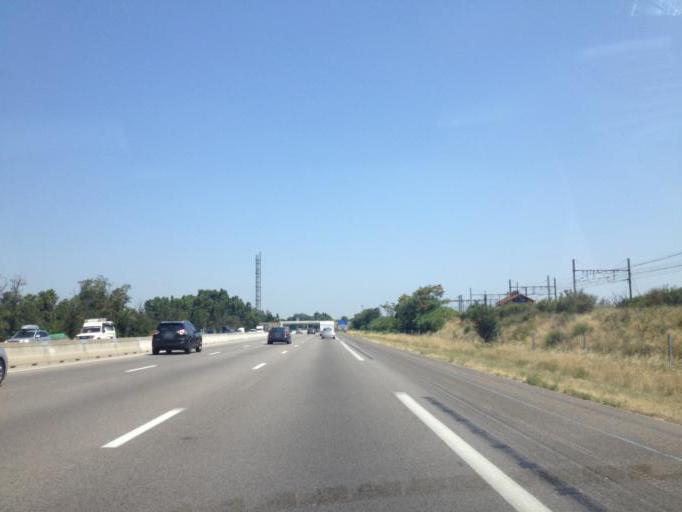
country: FR
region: Rhone-Alpes
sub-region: Departement de la Drome
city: Etoile-sur-Rhone
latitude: 44.8494
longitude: 4.8657
